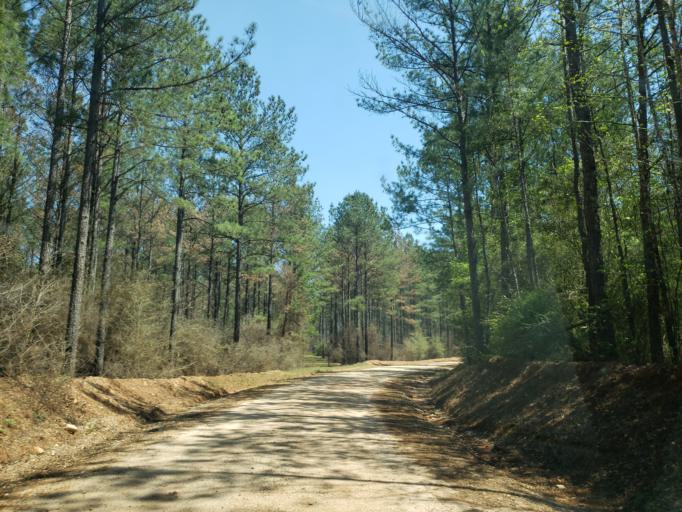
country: US
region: Alabama
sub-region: Tallapoosa County
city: Camp Hill
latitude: 32.6498
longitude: -85.6510
